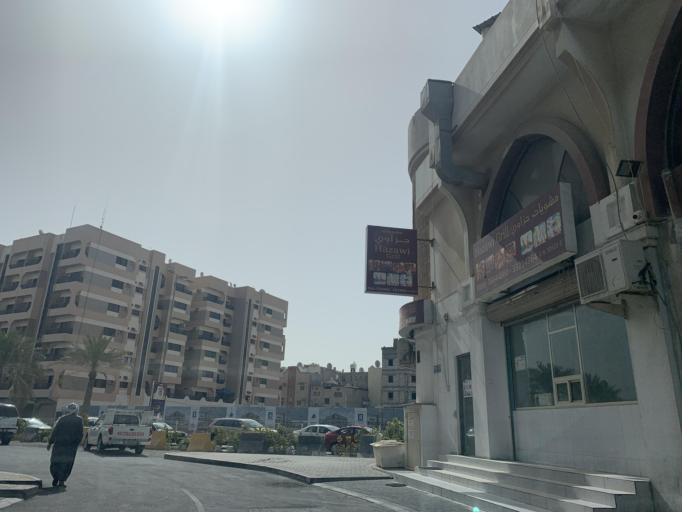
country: BH
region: Manama
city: Manama
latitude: 26.2188
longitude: 50.5682
